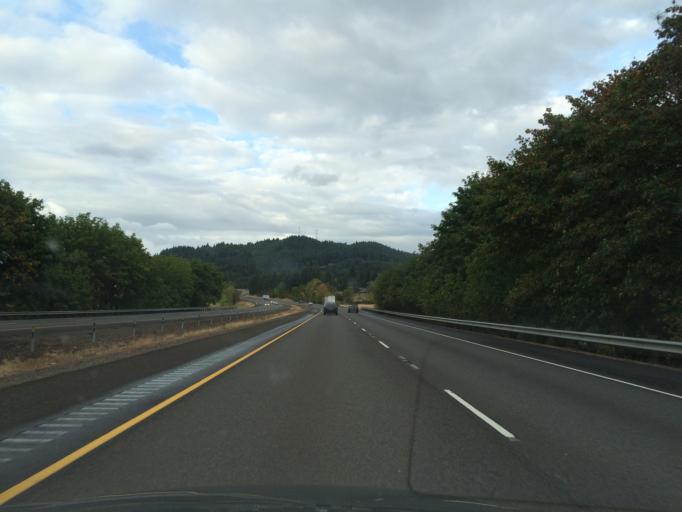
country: US
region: Oregon
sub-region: Lane County
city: Cottage Grove
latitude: 43.7666
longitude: -123.0697
